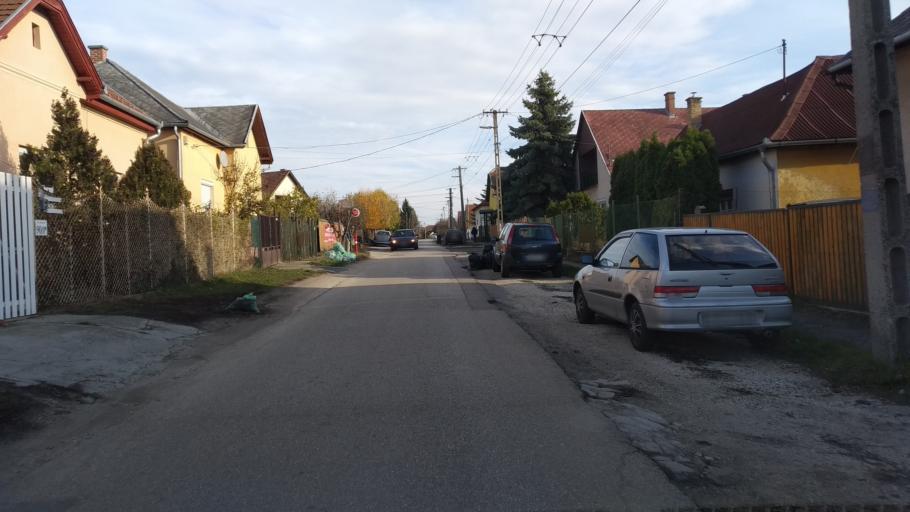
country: HU
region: Pest
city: Gyomro
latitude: 47.4309
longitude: 19.3869
